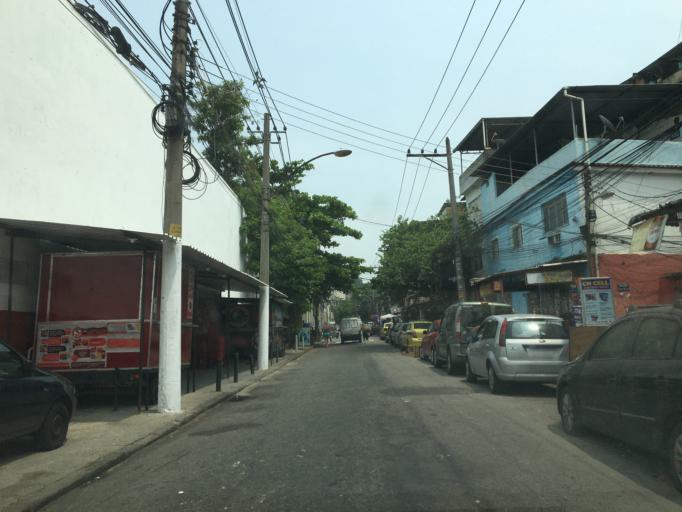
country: BR
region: Rio de Janeiro
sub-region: Rio De Janeiro
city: Rio de Janeiro
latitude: -22.8889
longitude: -43.2275
